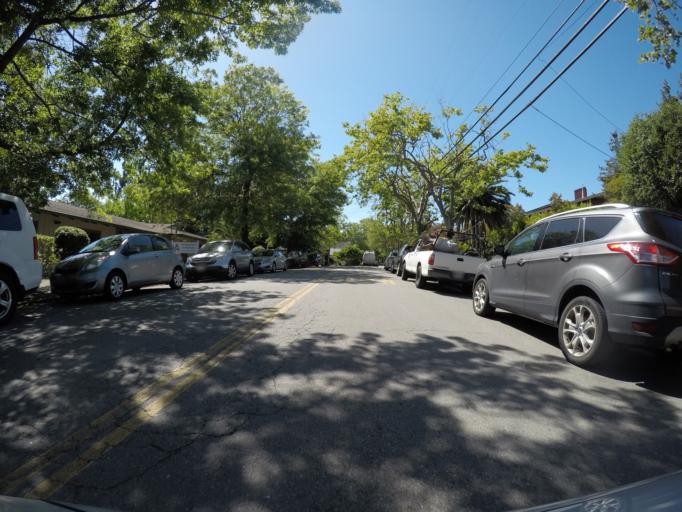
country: US
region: California
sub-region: Marin County
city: San Rafael
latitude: 37.9724
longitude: -122.5163
